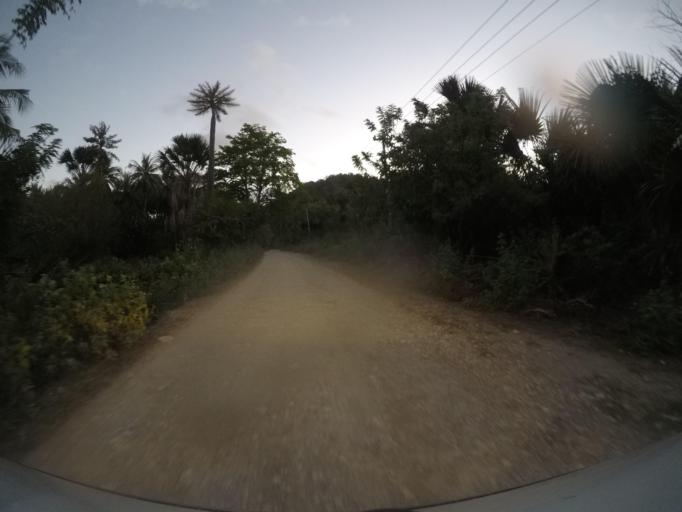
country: TL
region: Viqueque
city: Viqueque
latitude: -8.7910
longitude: 126.6267
